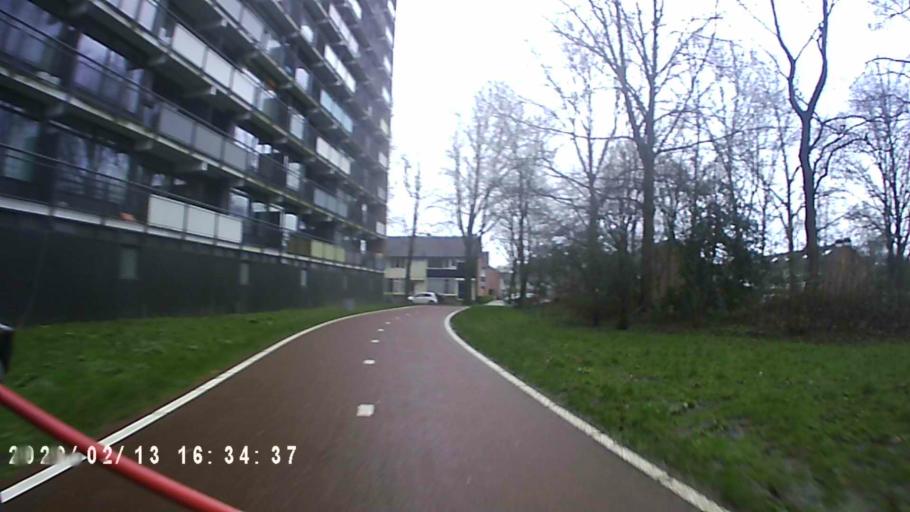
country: NL
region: Groningen
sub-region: Gemeente Groningen
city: Korrewegwijk
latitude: 53.2327
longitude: 6.5244
